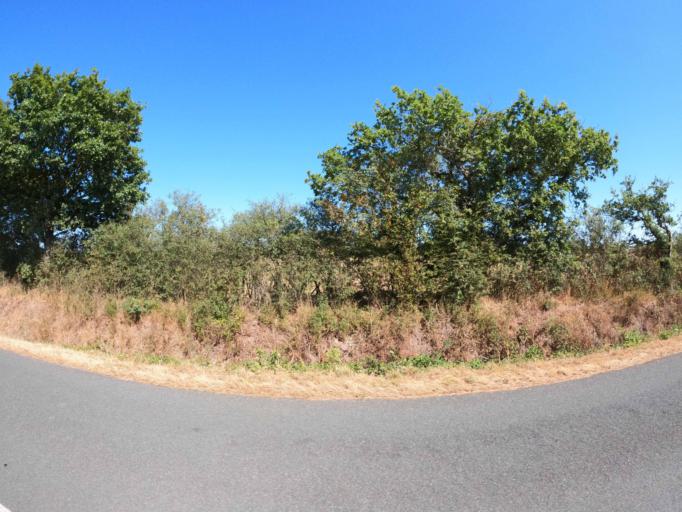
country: FR
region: Pays de la Loire
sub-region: Departement de la Vendee
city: Saint-Aubin-des-Ormeaux
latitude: 46.9826
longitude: -1.0505
